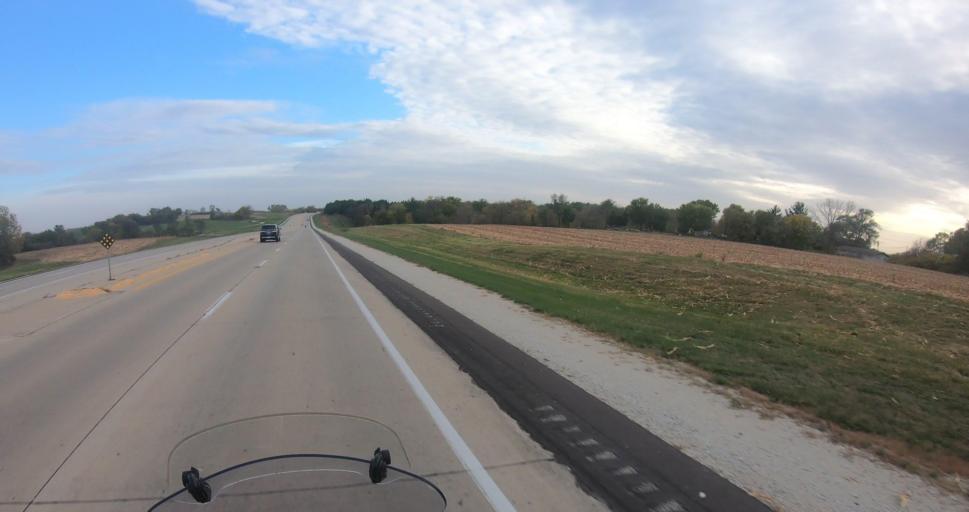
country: US
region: Iowa
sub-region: Polk County
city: West Des Moines
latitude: 41.5385
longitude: -93.7011
